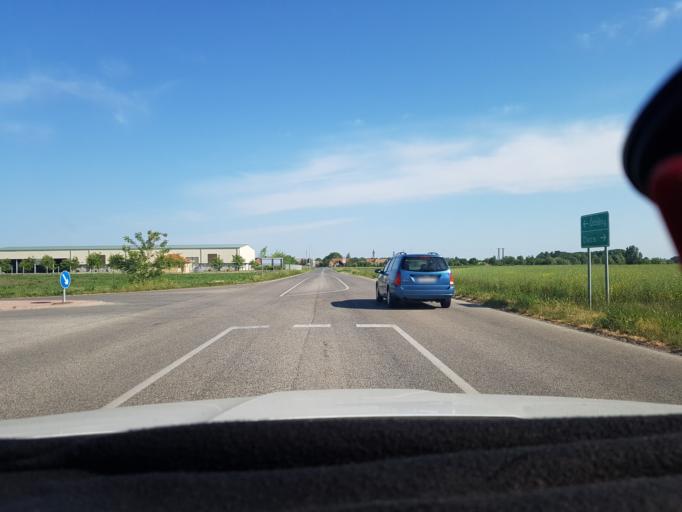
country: HU
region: Tolna
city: Ocseny
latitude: 46.3044
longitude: 18.7595
